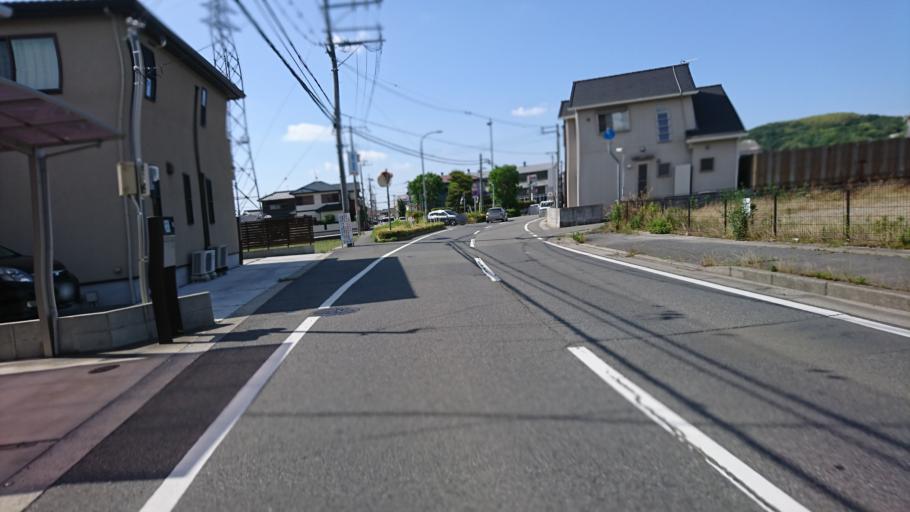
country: JP
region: Hyogo
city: Shirahamacho-usazakiminami
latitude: 34.7899
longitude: 134.7508
